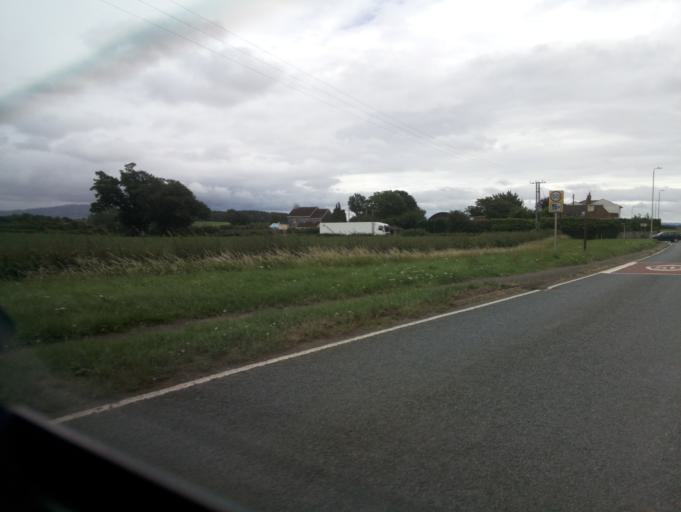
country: GB
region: England
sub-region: Worcestershire
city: Upton upon Severn
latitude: 52.0721
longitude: -2.1994
